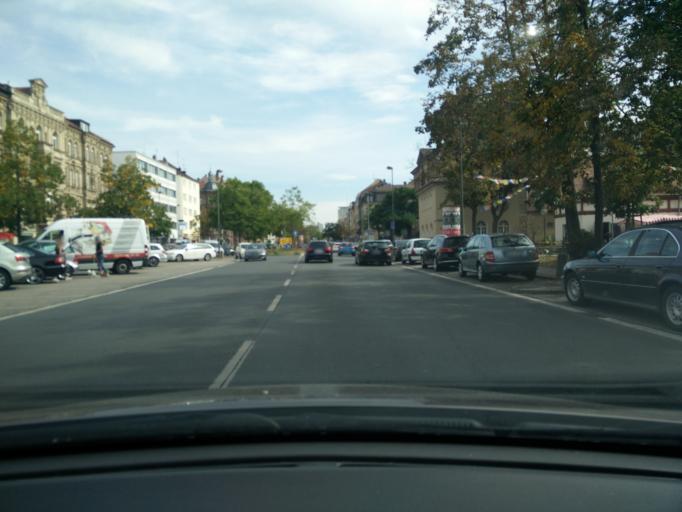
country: DE
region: Bavaria
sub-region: Regierungsbezirk Mittelfranken
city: Wetzendorf
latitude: 49.4517
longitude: 11.0530
